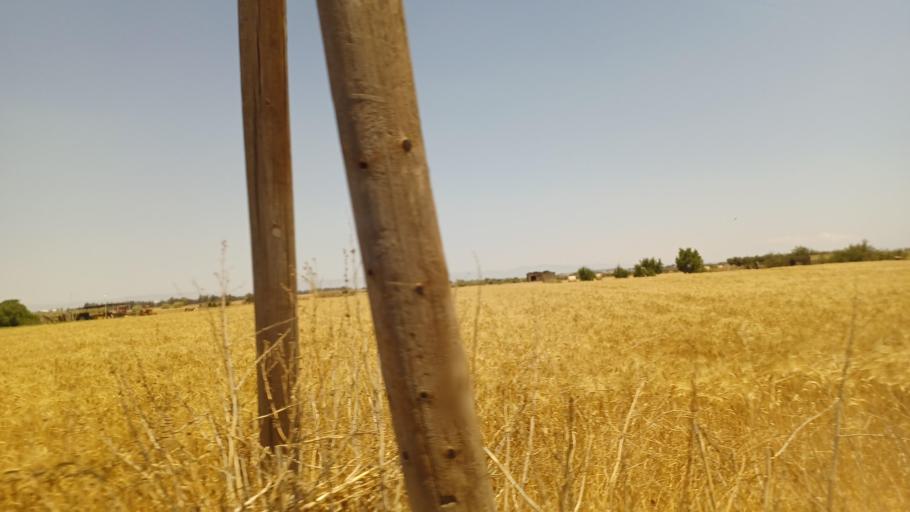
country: CY
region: Ammochostos
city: Achna
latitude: 35.0638
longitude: 33.8124
